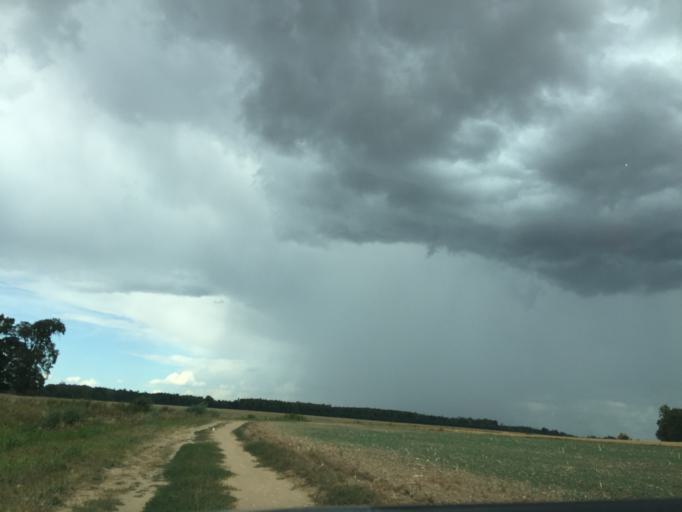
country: LT
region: Siauliu apskritis
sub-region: Joniskis
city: Joniskis
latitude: 56.2905
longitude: 23.7258
